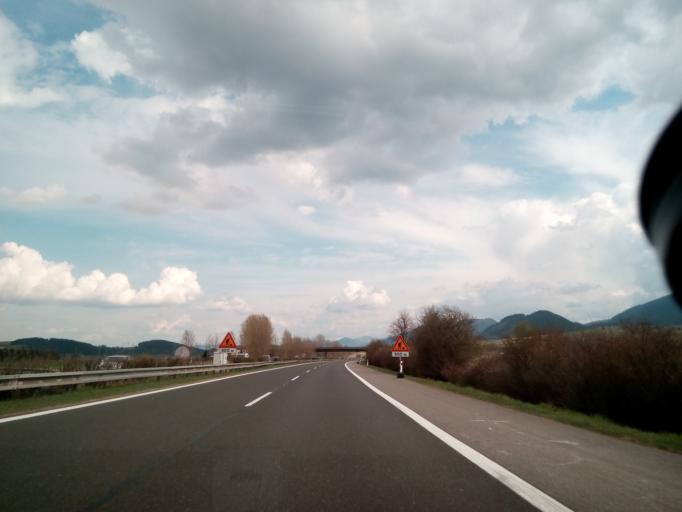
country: SK
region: Zilinsky
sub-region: Okres Liptovsky Mikulas
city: Liptovsky Mikulas
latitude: 49.0659
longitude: 19.6433
